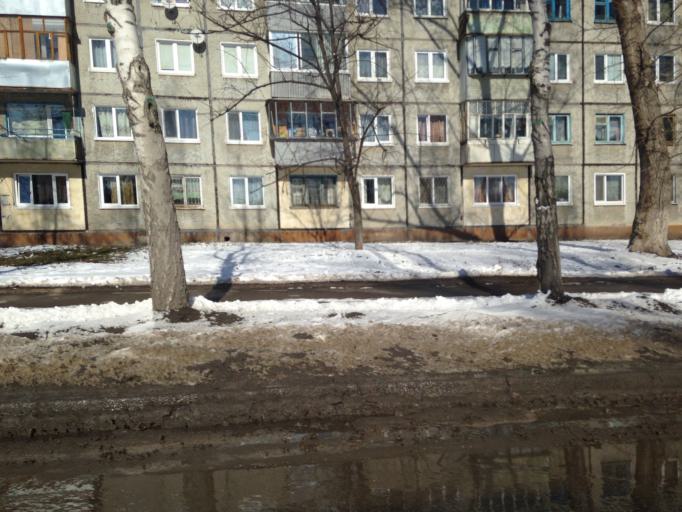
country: RU
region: Ulyanovsk
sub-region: Ulyanovskiy Rayon
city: Ulyanovsk
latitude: 54.3310
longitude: 48.4916
